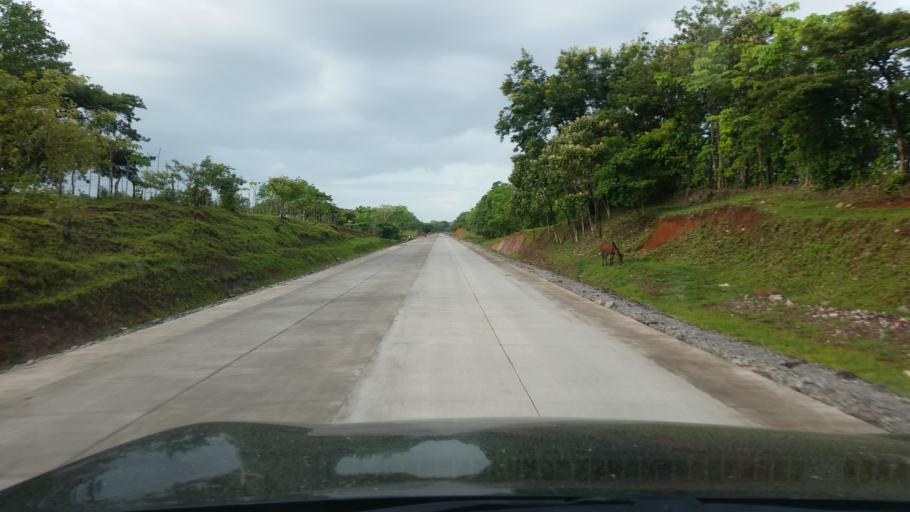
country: NI
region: Matagalpa
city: Rio Blanco
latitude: 13.1254
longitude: -85.0501
